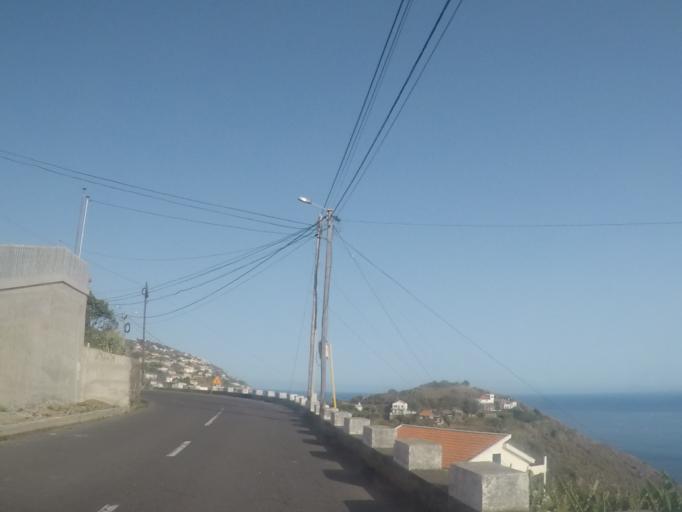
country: PT
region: Madeira
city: Ribeira Brava
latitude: 32.6769
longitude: -17.0699
